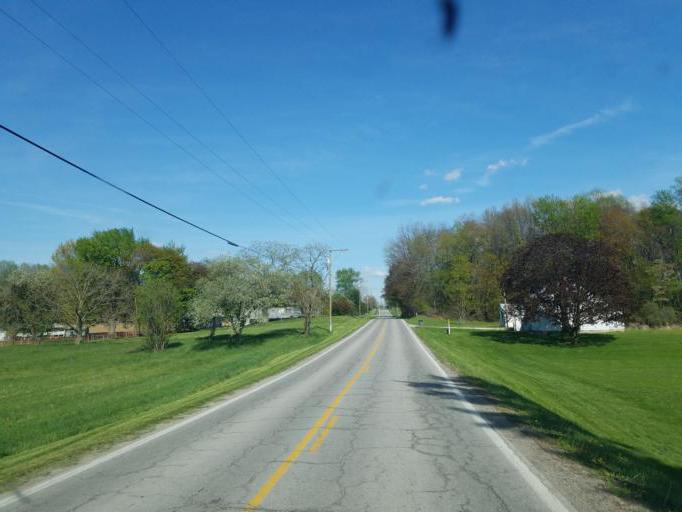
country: US
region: Ohio
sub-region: Huron County
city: Plymouth
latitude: 40.9954
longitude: -82.7013
